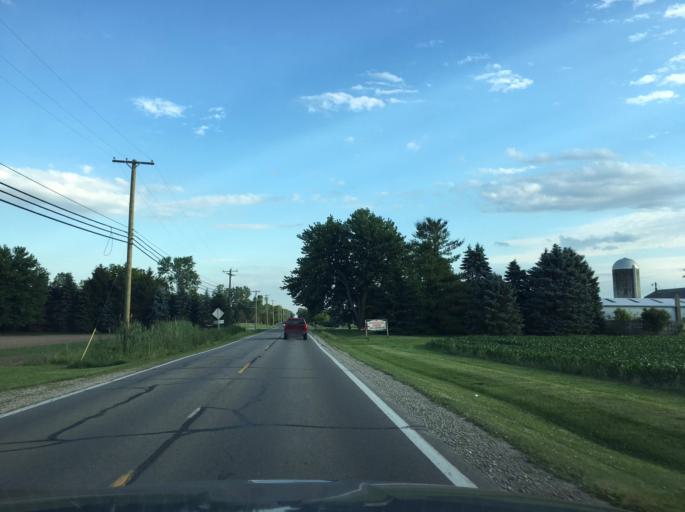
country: US
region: Michigan
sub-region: Macomb County
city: Romeo
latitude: 42.7447
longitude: -82.9605
